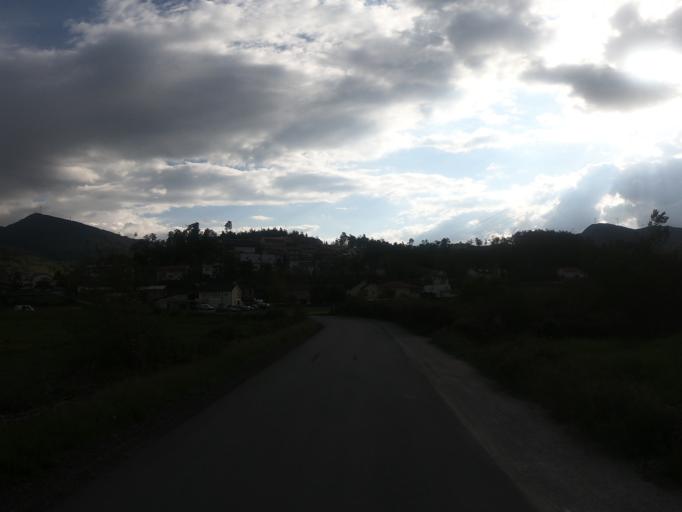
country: PT
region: Vila Real
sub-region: Santa Marta de Penaguiao
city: Santa Marta de Penaguiao
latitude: 41.2957
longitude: -7.8744
